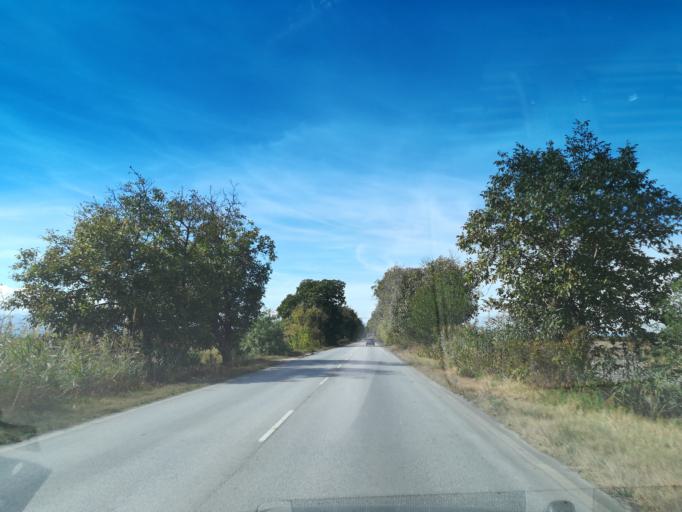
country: BG
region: Plovdiv
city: Stamboliyski
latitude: 42.1351
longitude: 24.6305
